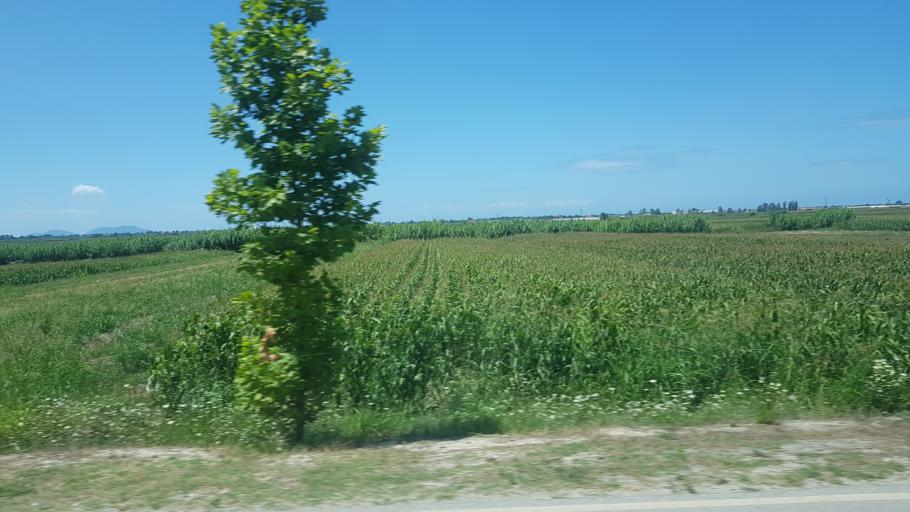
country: AL
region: Fier
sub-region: Rrethi i Fierit
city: Frakulla e Madhe
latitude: 40.6572
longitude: 19.4907
